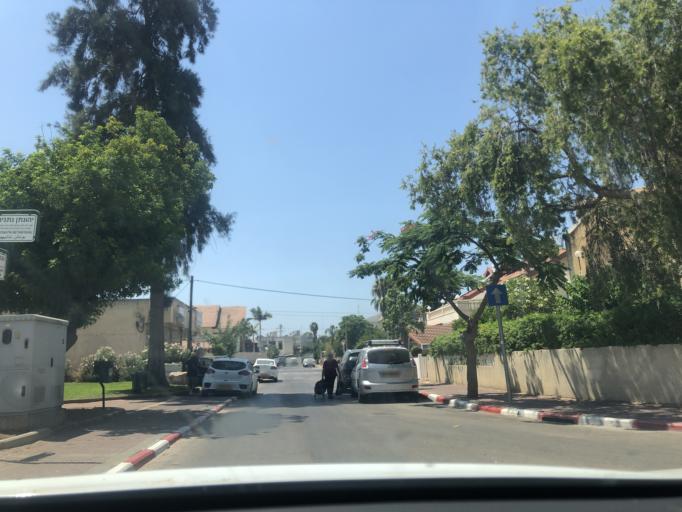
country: IL
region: Central District
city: Lod
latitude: 31.9378
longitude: 34.8881
